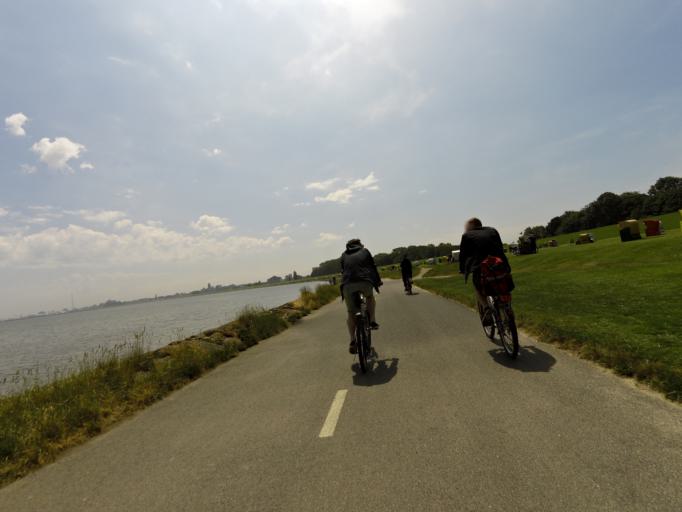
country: DE
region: Lower Saxony
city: Cuxhaven
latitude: 53.8884
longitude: 8.6832
